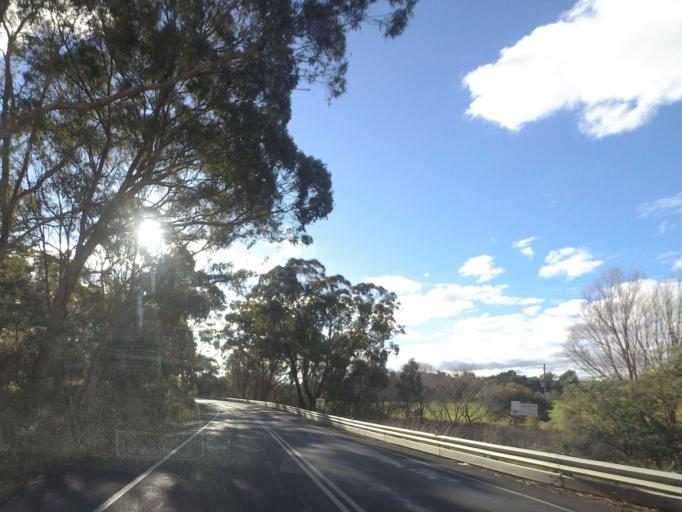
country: AU
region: Victoria
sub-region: Mount Alexander
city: Castlemaine
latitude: -37.1018
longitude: 144.2961
